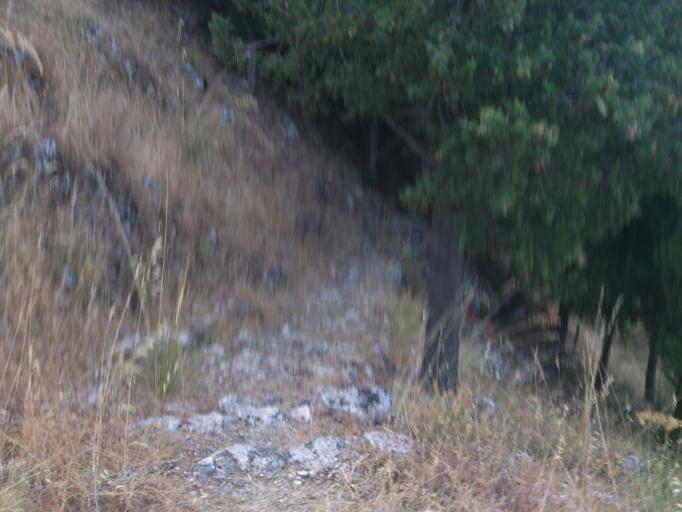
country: IT
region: Calabria
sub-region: Provincia di Reggio Calabria
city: Pazzano
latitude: 38.4711
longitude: 16.4502
